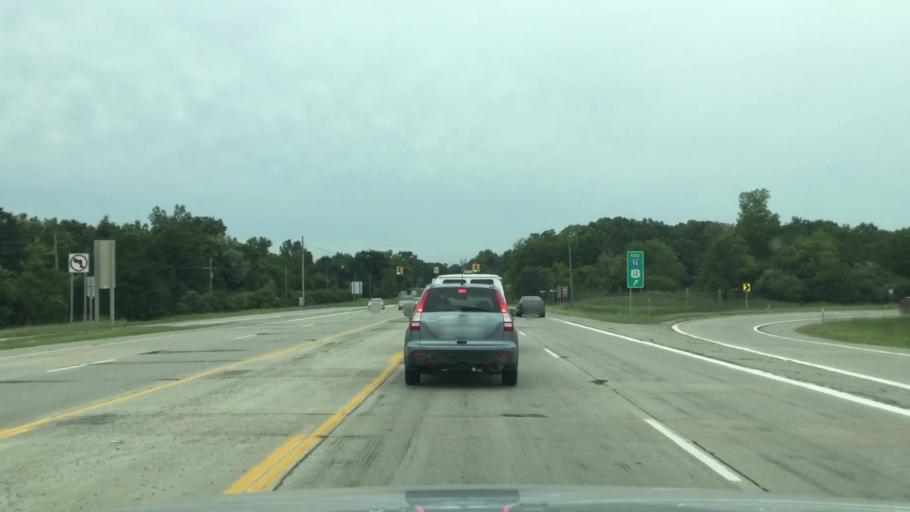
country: US
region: Michigan
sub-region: Washtenaw County
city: Ypsilanti
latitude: 42.2229
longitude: -83.6543
